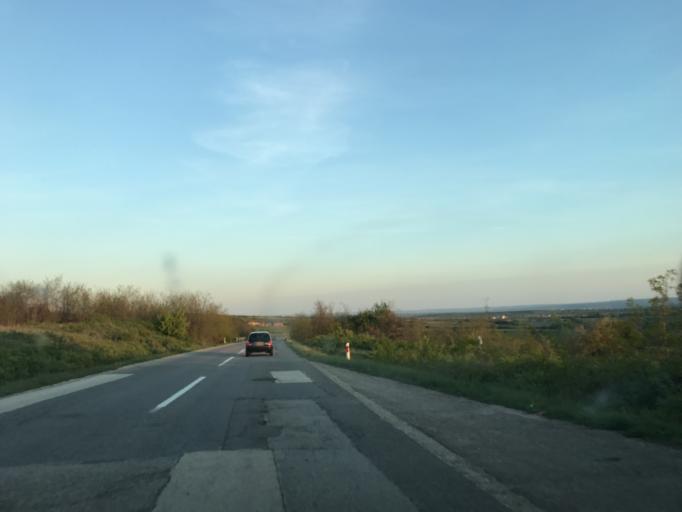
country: RO
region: Mehedinti
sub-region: Comuna Gogosu
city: Ostrovu Mare
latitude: 44.3192
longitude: 22.4947
